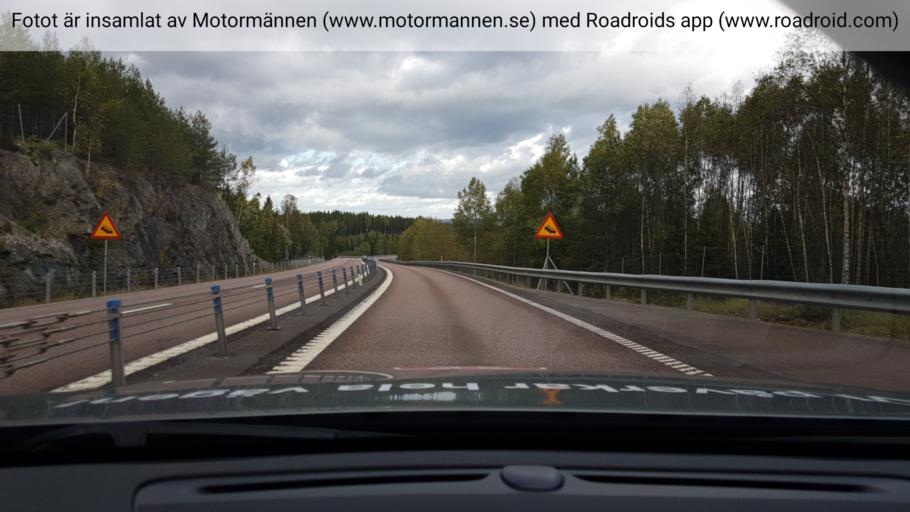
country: SE
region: Vaermland
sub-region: Arjangs Kommun
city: Toecksfors
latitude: 59.4911
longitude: 11.7722
